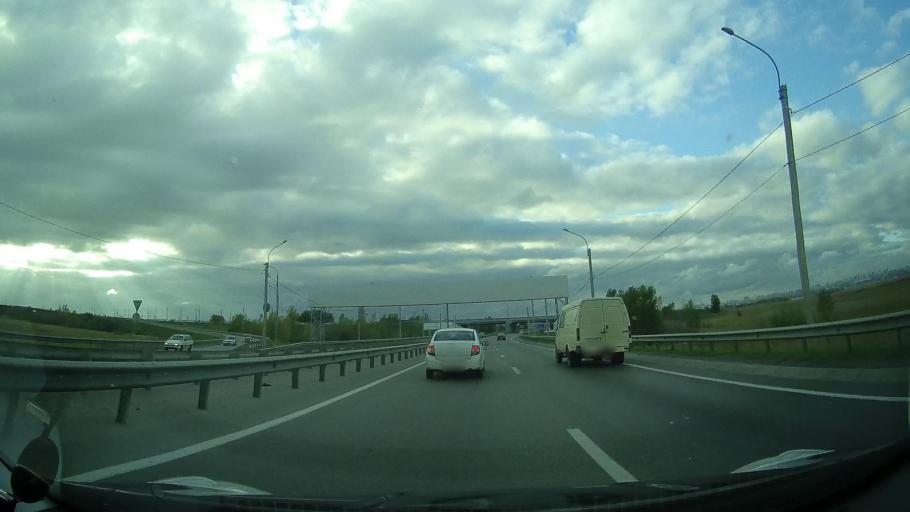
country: RU
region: Rostov
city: Bataysk
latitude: 47.1682
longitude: 39.7504
